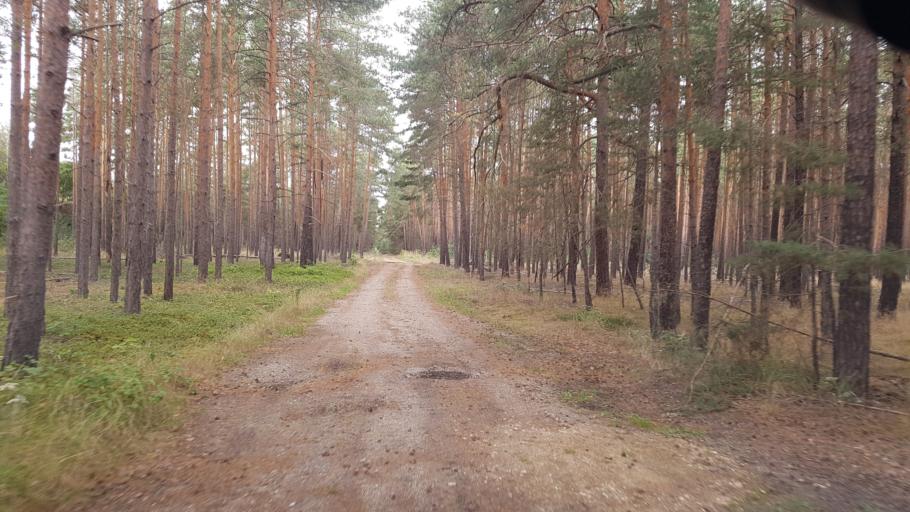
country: DE
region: Brandenburg
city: Ruckersdorf
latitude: 51.5769
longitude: 13.5944
